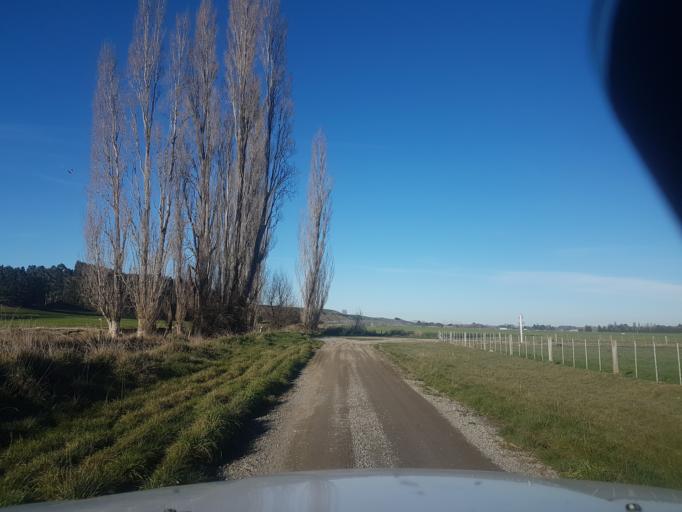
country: NZ
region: Canterbury
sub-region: Timaru District
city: Pleasant Point
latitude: -44.2224
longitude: 171.0520
